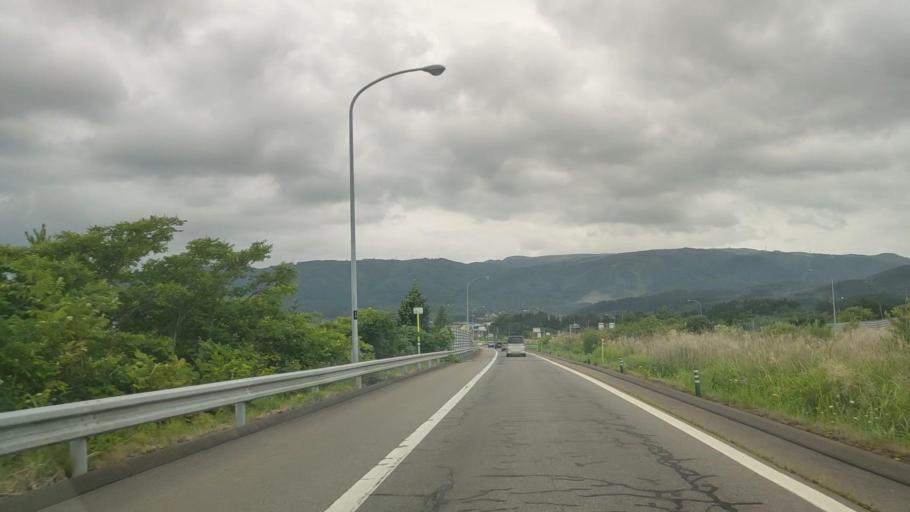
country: JP
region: Hokkaido
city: Nanae
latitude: 41.9223
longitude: 140.6714
